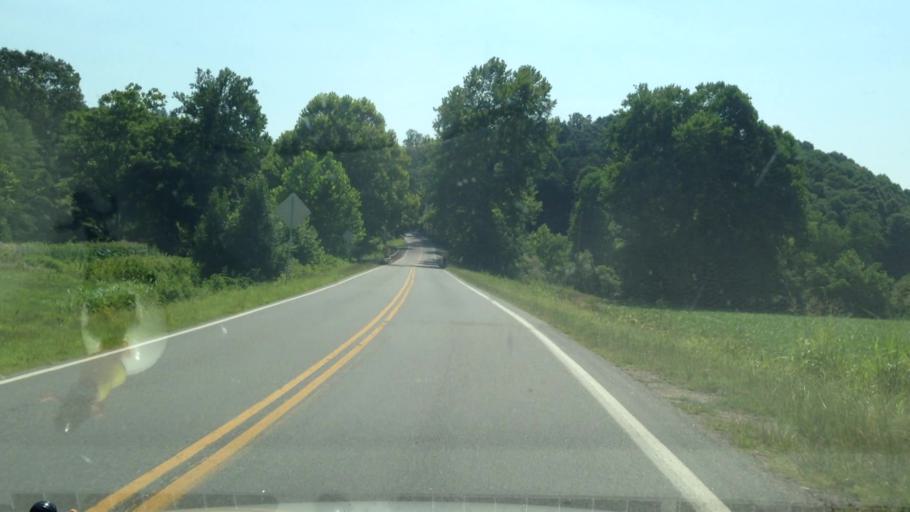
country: US
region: Virginia
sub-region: Patrick County
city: Stuart
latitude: 36.5769
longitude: -80.3788
